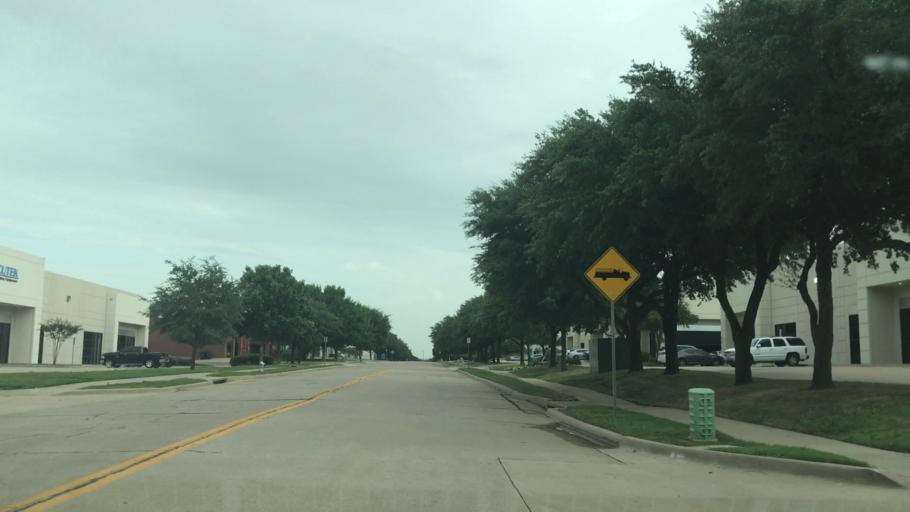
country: US
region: Texas
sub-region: Dallas County
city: Coppell
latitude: 32.9160
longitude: -97.0027
